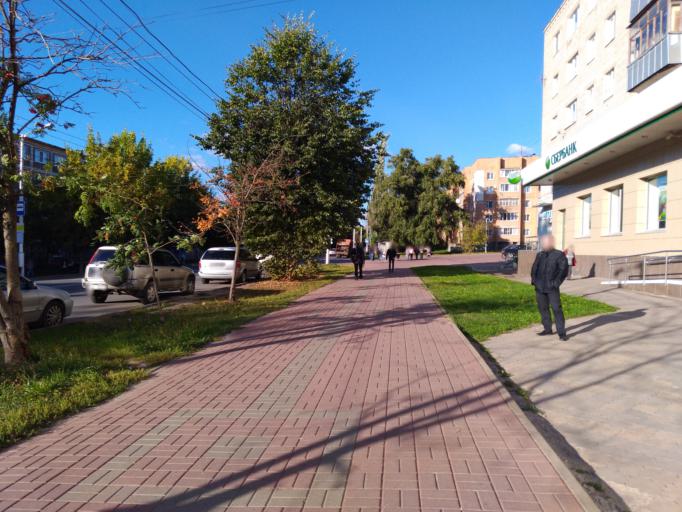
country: RU
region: Kaluga
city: Kaluga
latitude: 54.5282
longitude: 36.2740
